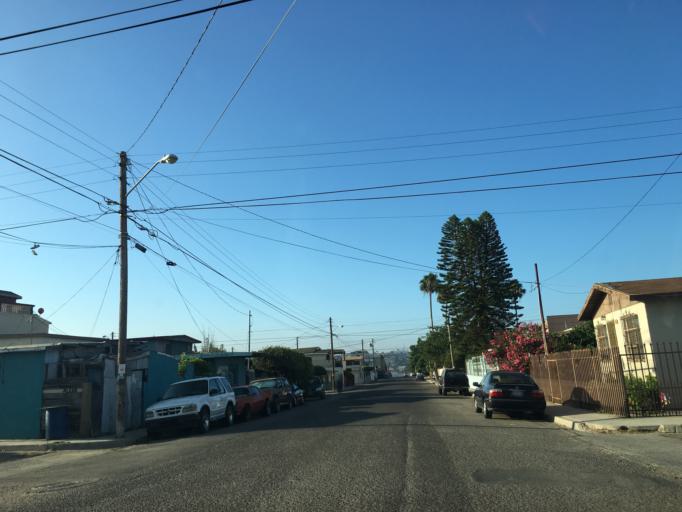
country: US
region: California
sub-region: San Diego County
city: Imperial Beach
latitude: 32.5349
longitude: -117.0785
